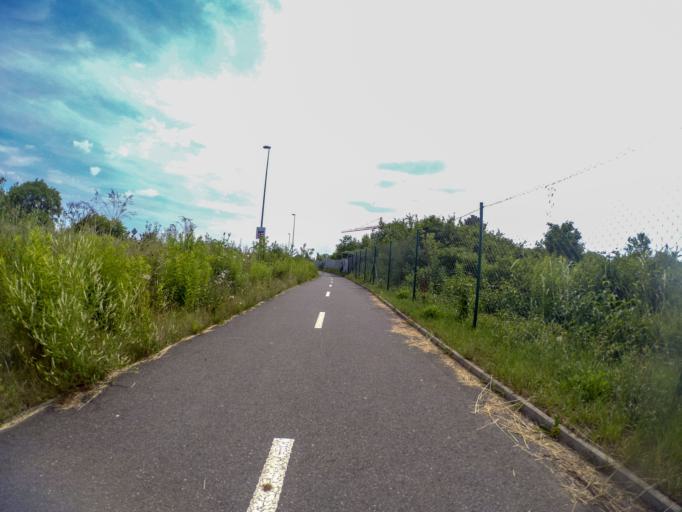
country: CZ
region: Praha
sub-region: Praha 19
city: Kbely
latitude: 50.1342
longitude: 14.5351
